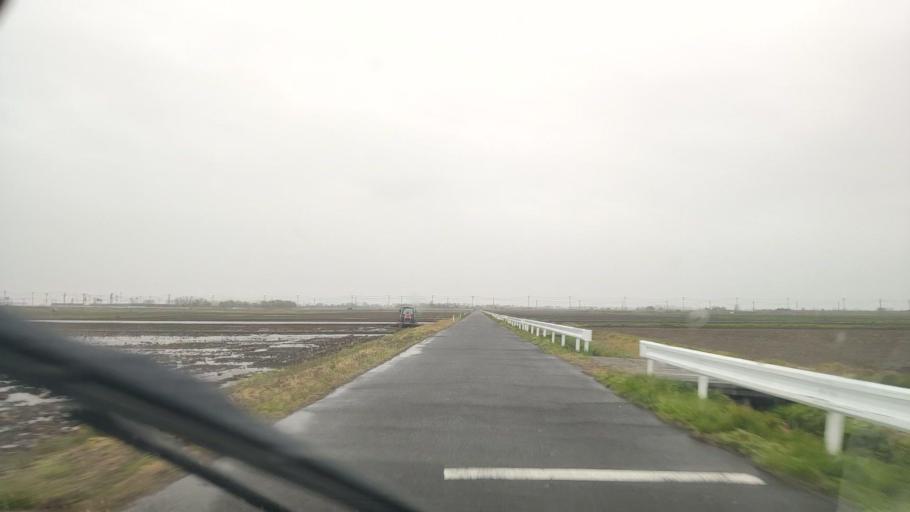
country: JP
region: Akita
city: Noshiromachi
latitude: 40.1019
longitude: 139.9977
